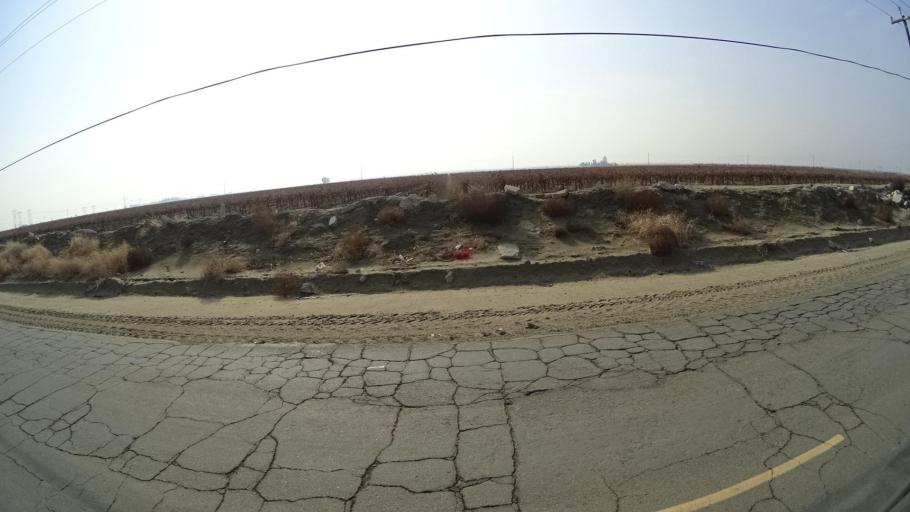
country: US
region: California
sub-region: Kern County
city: Arvin
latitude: 35.0929
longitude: -118.8942
